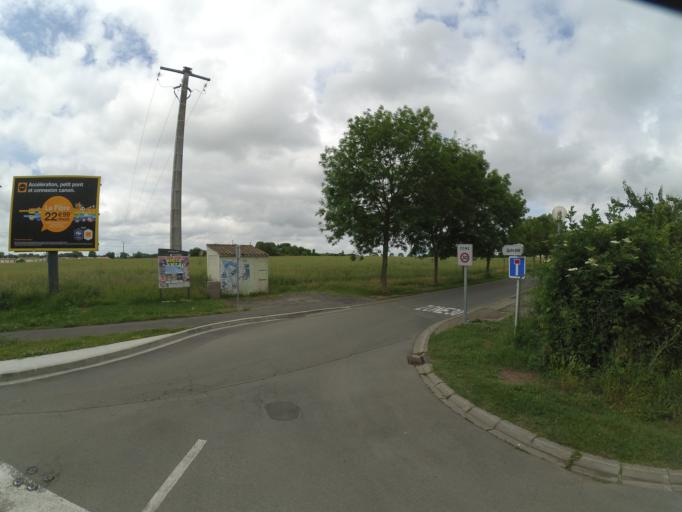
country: FR
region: Poitou-Charentes
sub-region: Departement de la Charente-Maritime
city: Breuil-Magne
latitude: 45.9610
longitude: -0.9697
